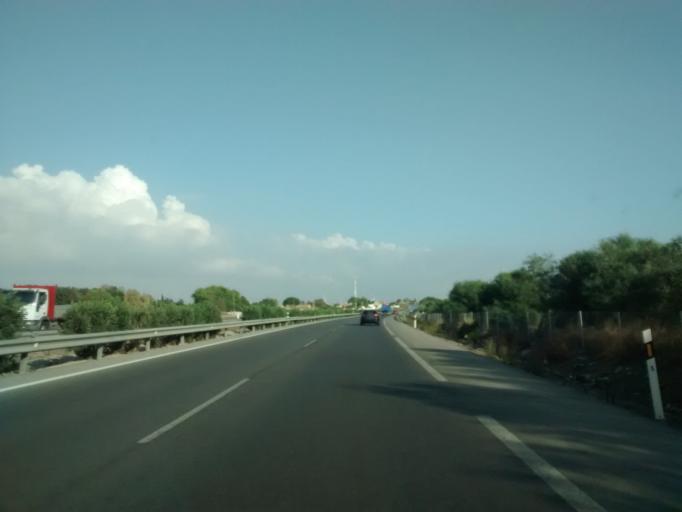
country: ES
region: Andalusia
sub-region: Provincia de Cadiz
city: Chiclana de la Frontera
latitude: 36.4411
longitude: -6.1303
